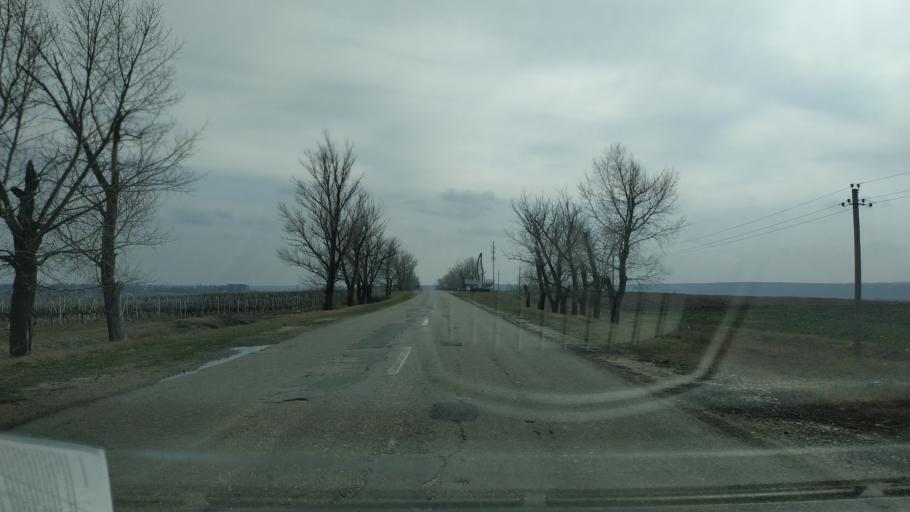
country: MD
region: Gagauzia
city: Vulcanesti
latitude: 45.7039
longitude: 28.4014
